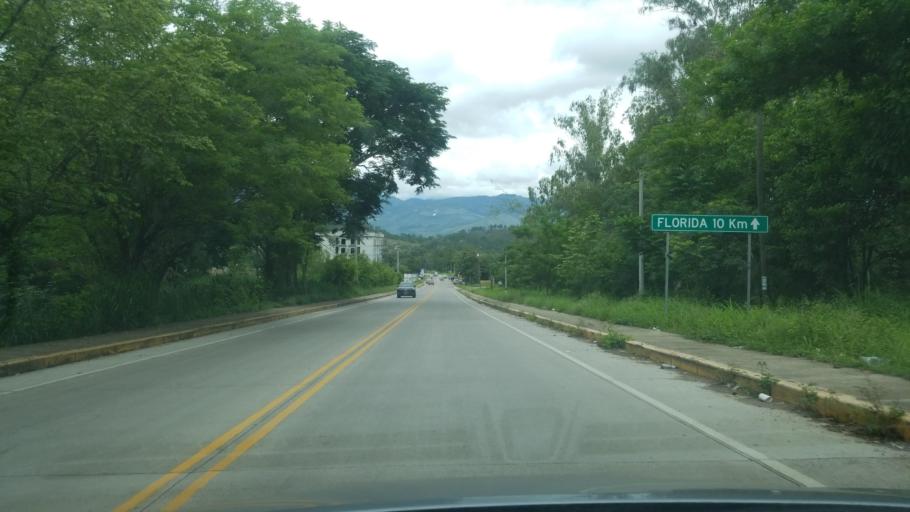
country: HN
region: Copan
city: La Entrada
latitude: 15.0670
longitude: -88.7602
